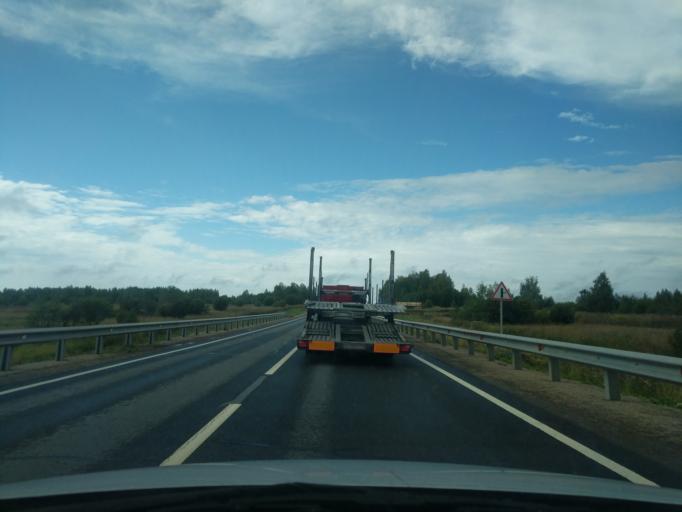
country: RU
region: Kostroma
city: Sudislavl'
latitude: 57.8173
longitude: 41.9488
